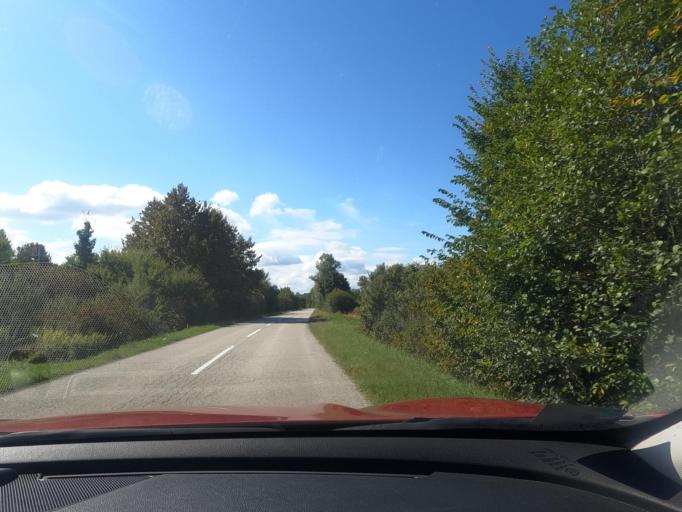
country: BA
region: Federation of Bosnia and Herzegovina
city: Vrnograc
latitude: 45.2521
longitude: 15.9441
